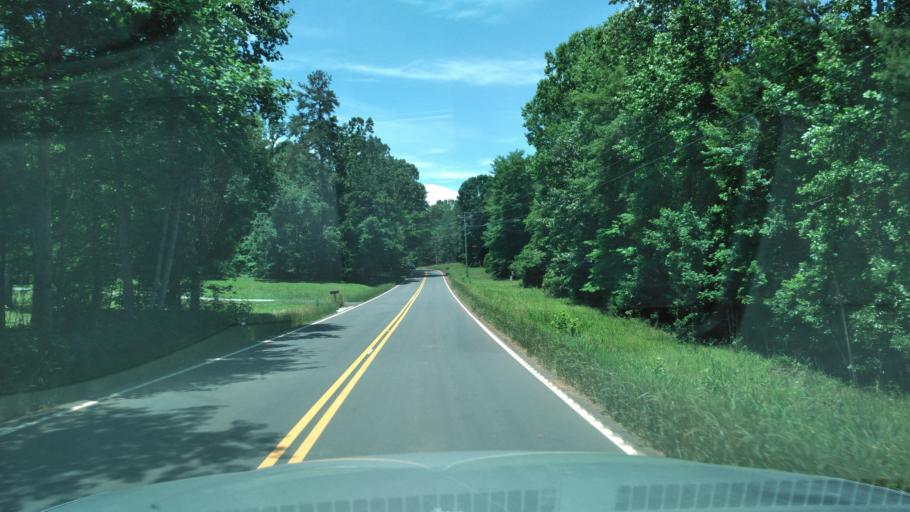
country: US
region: South Carolina
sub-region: Greenwood County
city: Ware Shoals
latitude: 34.4255
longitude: -82.1336
